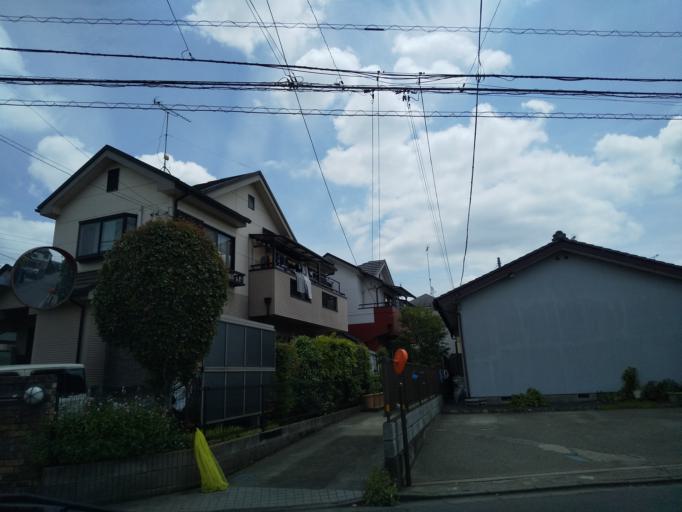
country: JP
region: Tokyo
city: Hachioji
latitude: 35.6789
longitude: 139.3204
